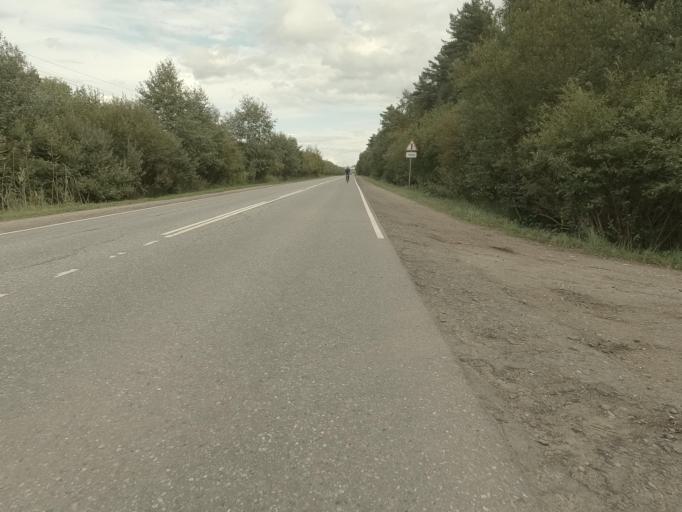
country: RU
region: Leningrad
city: Mga
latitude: 59.7613
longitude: 31.0039
